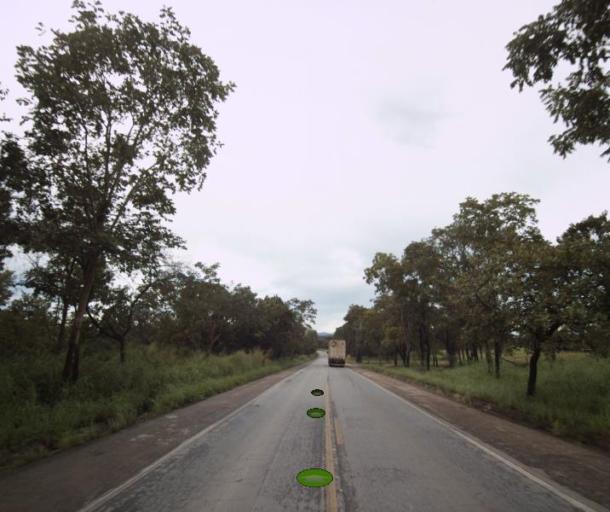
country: BR
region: Goias
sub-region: Porangatu
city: Porangatu
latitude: -13.6467
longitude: -49.0395
